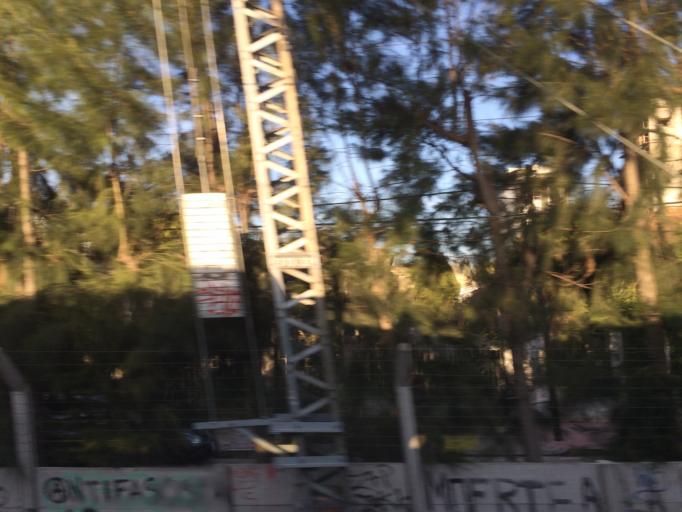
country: AR
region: Buenos Aires
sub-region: Partido de Lomas de Zamora
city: Lomas de Zamora
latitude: -34.7511
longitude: -58.3961
